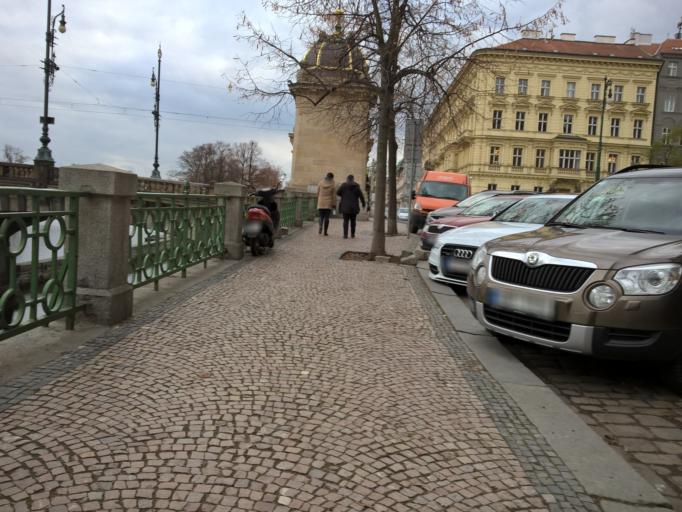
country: CZ
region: Praha
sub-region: Praha 1
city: Mala Strana
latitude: 50.0816
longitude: 14.4081
